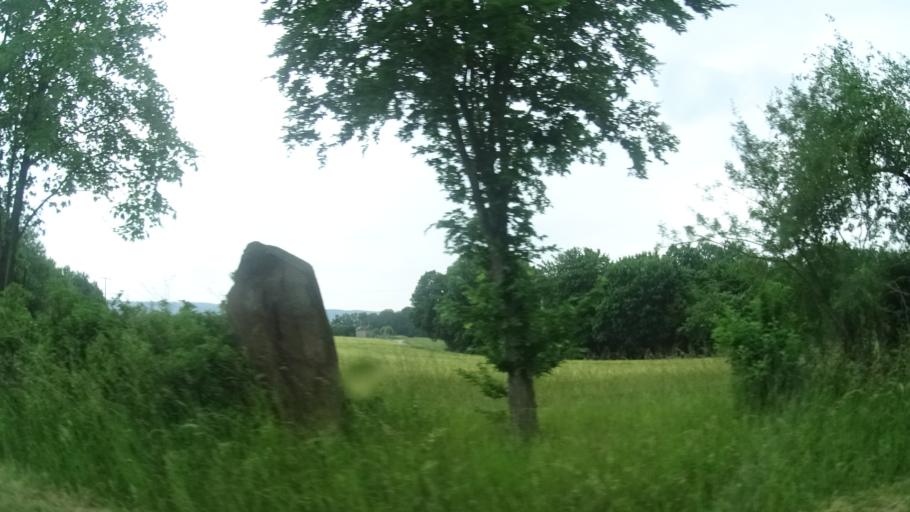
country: DE
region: Hesse
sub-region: Regierungsbezirk Kassel
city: Bad Salzschlirf
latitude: 50.6106
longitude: 9.5059
